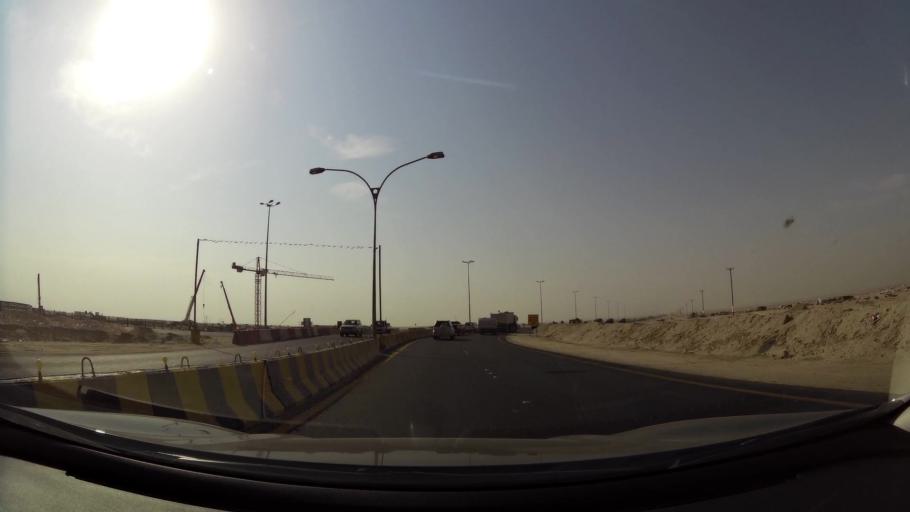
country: KW
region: Al Ahmadi
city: Al Ahmadi
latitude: 28.8874
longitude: 48.0835
